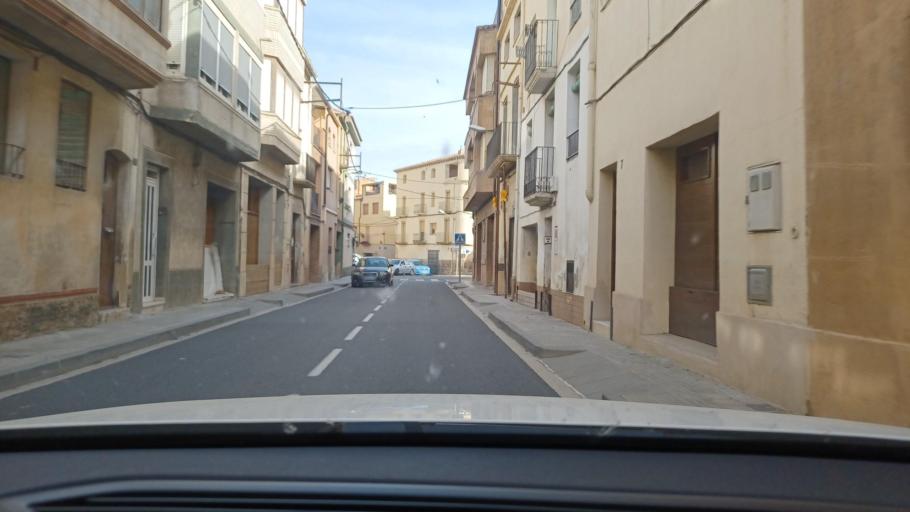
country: ES
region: Catalonia
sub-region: Provincia de Tarragona
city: Gandesa
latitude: 41.0517
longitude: 0.4398
